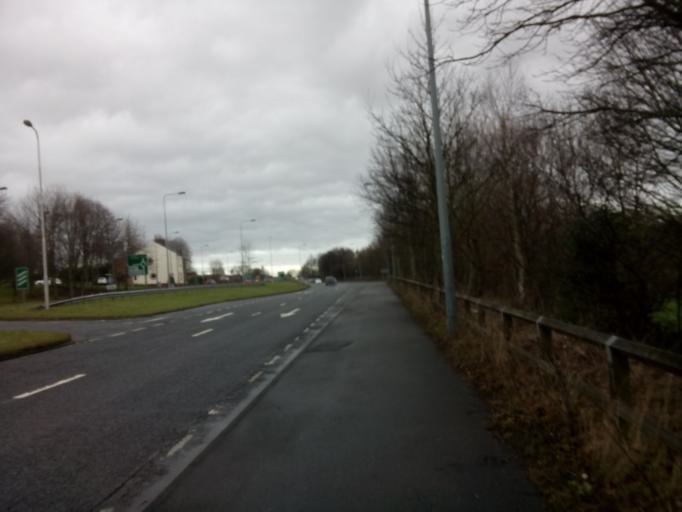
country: GB
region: England
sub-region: County Durham
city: Sacriston
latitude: 54.8209
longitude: -1.5923
